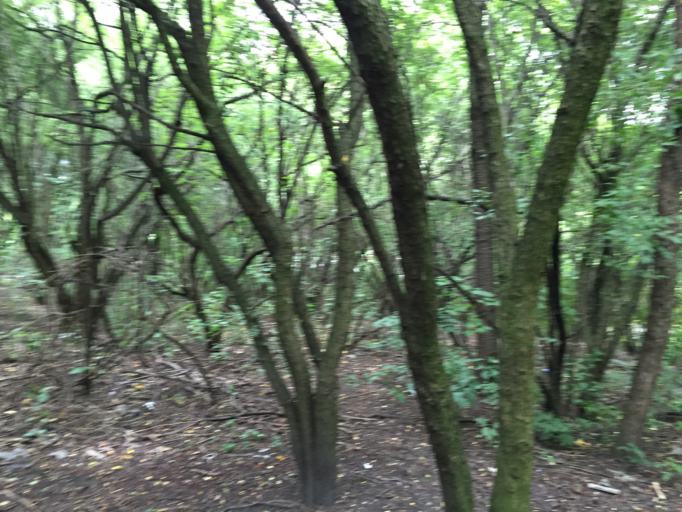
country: PL
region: Lesser Poland Voivodeship
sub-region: Krakow
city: Krakow
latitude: 50.0398
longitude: 19.9581
